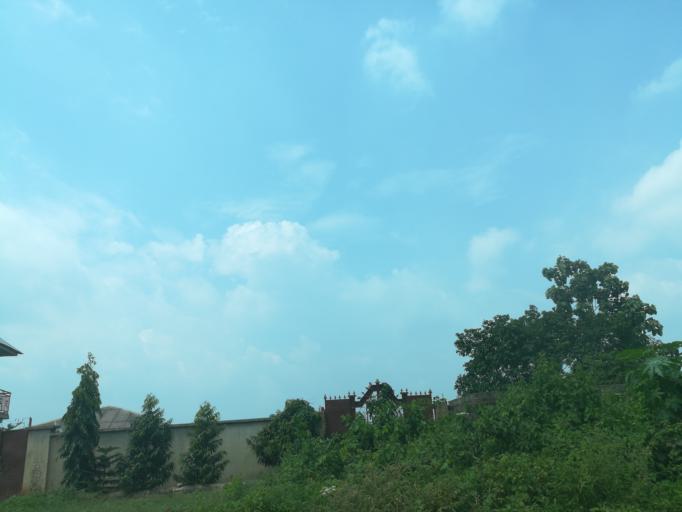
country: NG
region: Lagos
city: Ikorodu
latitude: 6.5995
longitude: 3.6281
